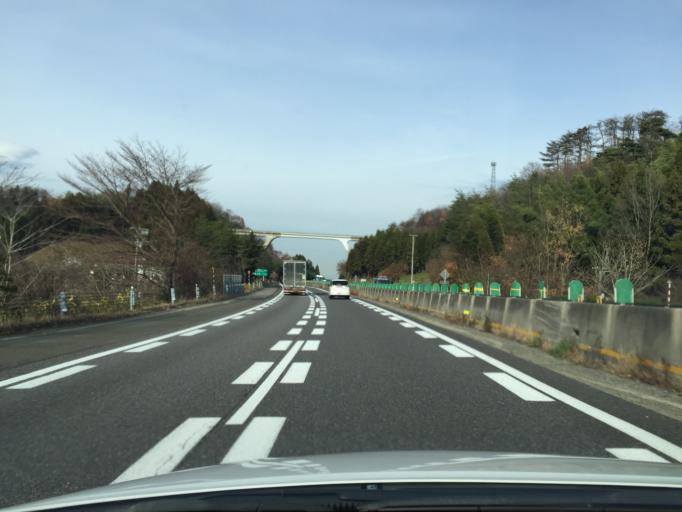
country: JP
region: Fukushima
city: Nihommatsu
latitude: 37.6329
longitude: 140.4340
